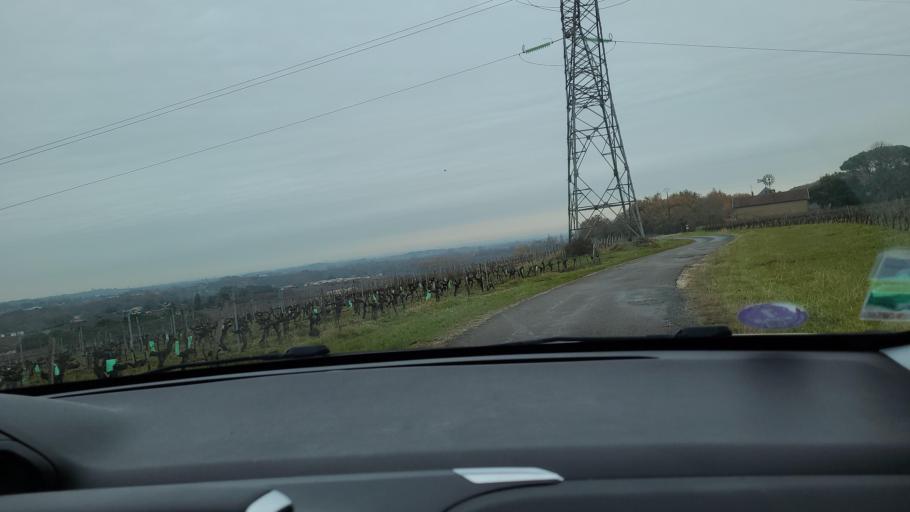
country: FR
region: Aquitaine
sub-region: Departement de la Gironde
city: Berson
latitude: 45.0843
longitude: -0.5535
